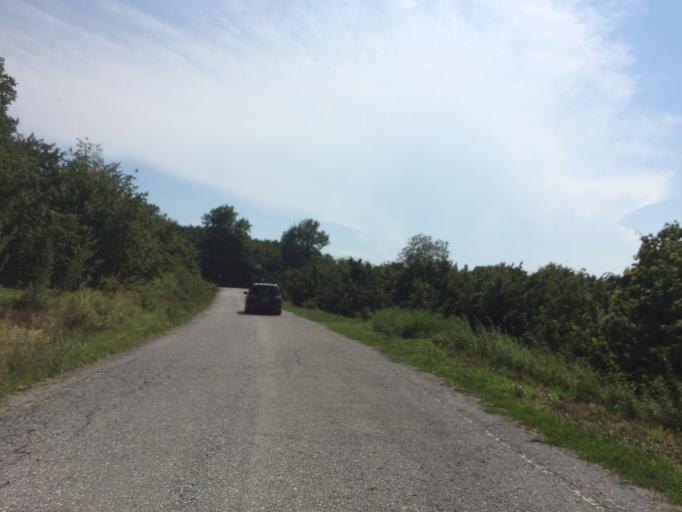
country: IT
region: Piedmont
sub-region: Provincia di Cuneo
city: Cravanzana
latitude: 44.5809
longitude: 8.1316
